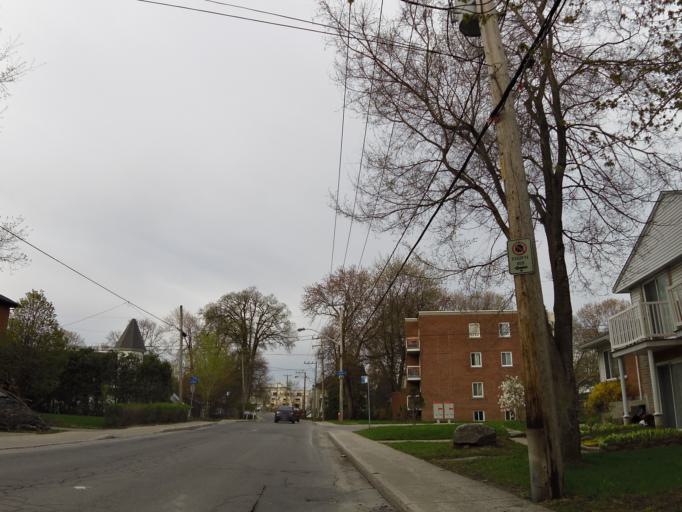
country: CA
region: Quebec
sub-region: Laval
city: Laval
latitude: 45.5443
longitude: -73.7116
